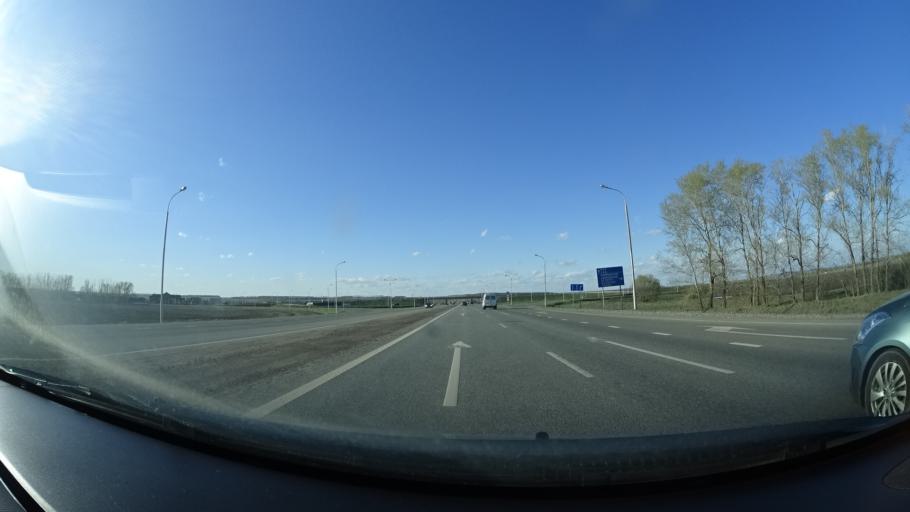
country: RU
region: Bashkortostan
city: Kabakovo
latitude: 54.4890
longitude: 55.9070
